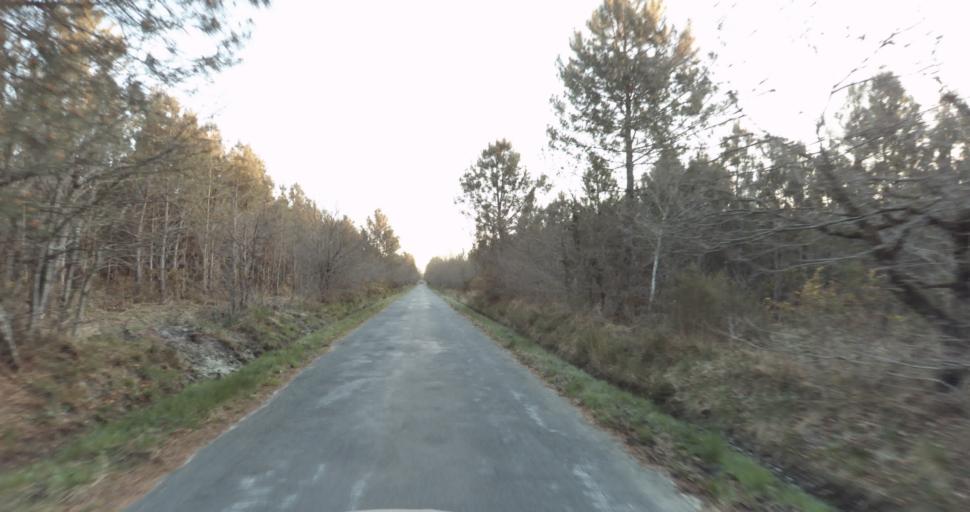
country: FR
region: Aquitaine
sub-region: Departement de la Gironde
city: Martignas-sur-Jalle
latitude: 44.8234
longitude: -0.7420
